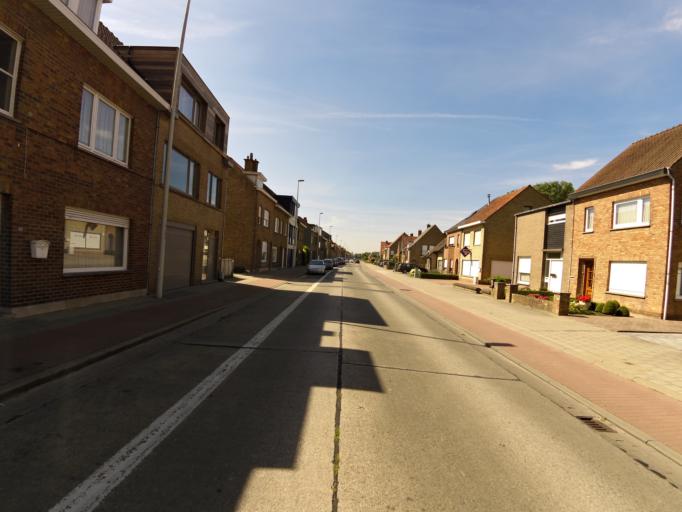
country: BE
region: Flanders
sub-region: Provincie West-Vlaanderen
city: Sint-Kruis
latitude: 51.2359
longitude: 3.2447
